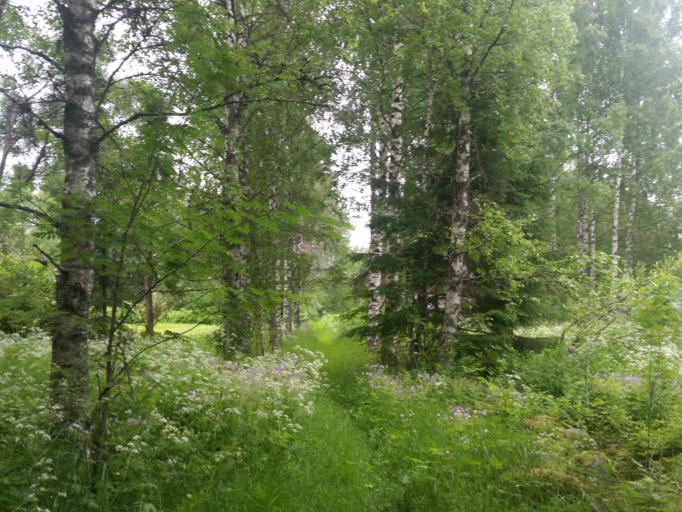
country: FI
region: Northern Savo
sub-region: Koillis-Savo
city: Kaavi
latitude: 62.9828
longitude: 28.7627
